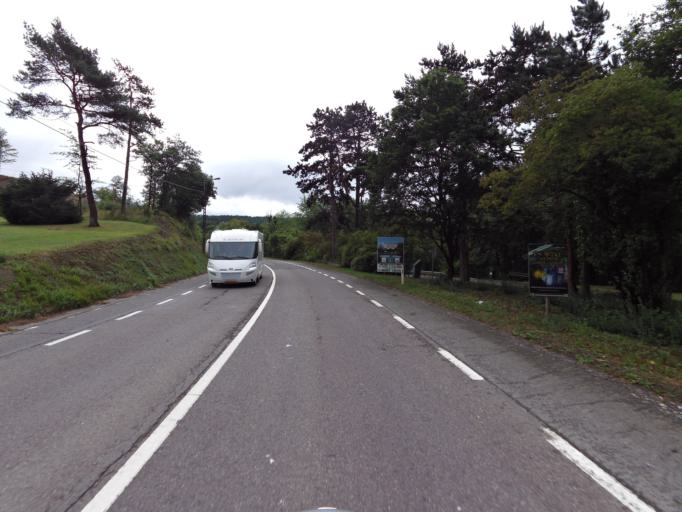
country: BE
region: Wallonia
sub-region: Province de Namur
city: Rochefort
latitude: 50.1313
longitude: 5.1877
